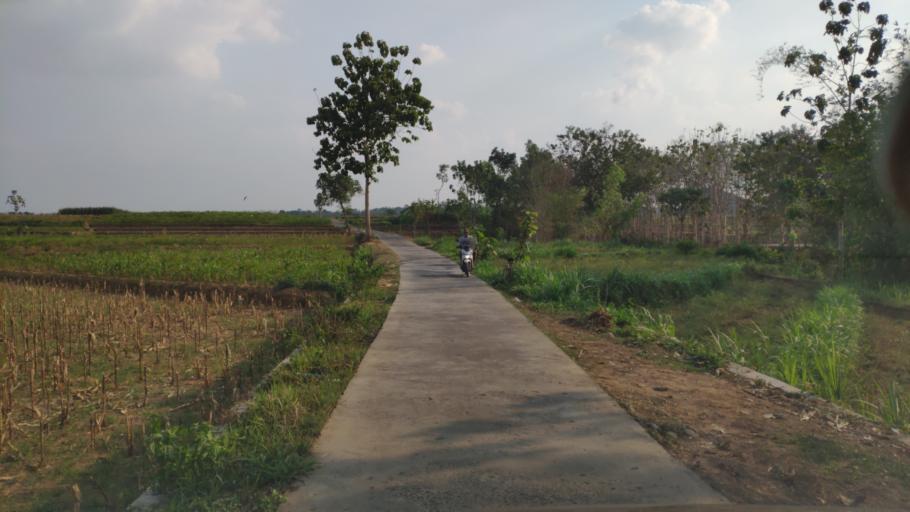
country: ID
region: Central Java
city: Guyangan
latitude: -6.9578
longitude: 111.1240
